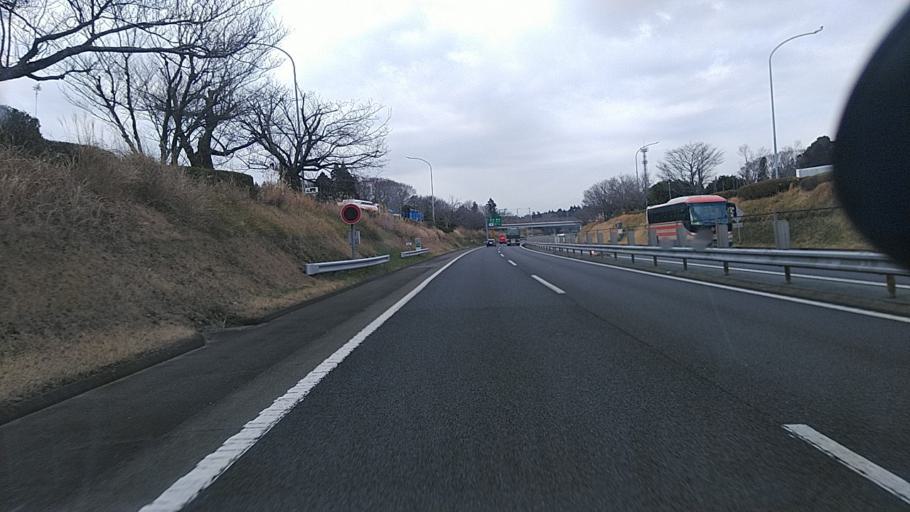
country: JP
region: Chiba
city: Oami
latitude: 35.5696
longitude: 140.2359
